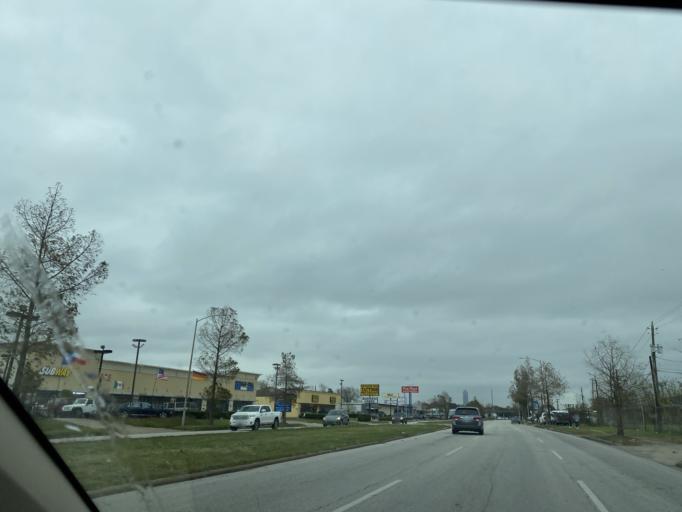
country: US
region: Texas
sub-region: Harris County
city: Piney Point Village
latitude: 29.7290
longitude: -95.5194
